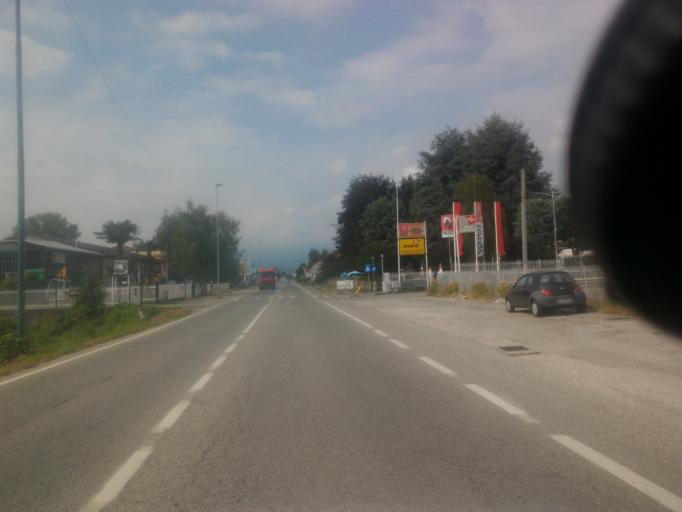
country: IT
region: Piedmont
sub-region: Provincia di Torino
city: Osasco
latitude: 44.8607
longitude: 7.3288
